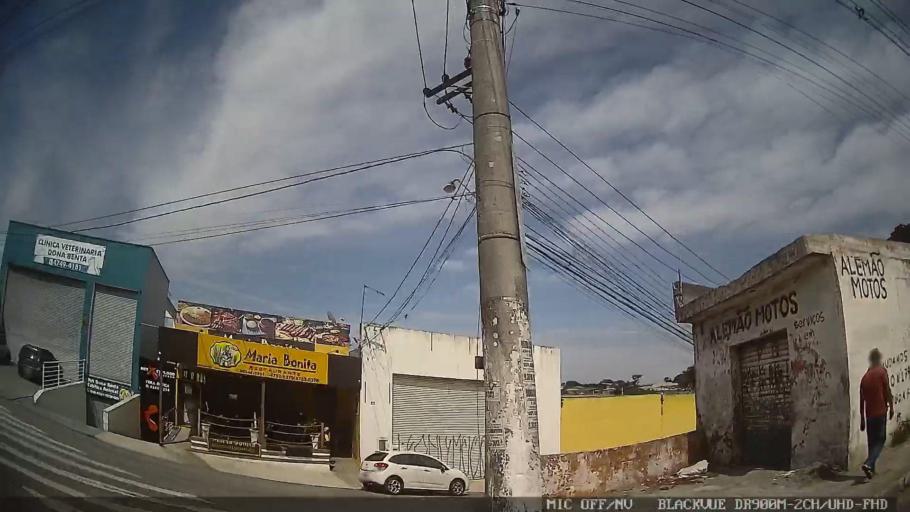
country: BR
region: Sao Paulo
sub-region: Suzano
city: Suzano
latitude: -23.5044
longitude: -46.3000
